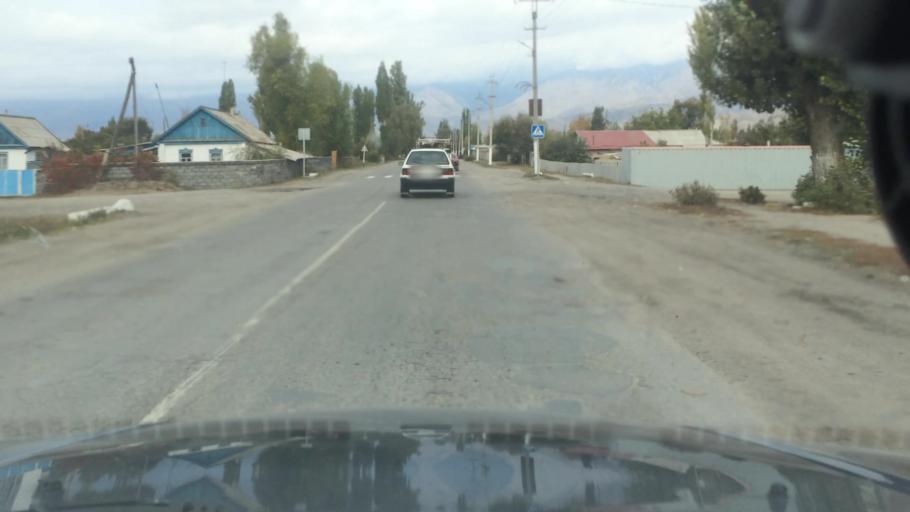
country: KG
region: Ysyk-Koel
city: Tyup
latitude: 42.7237
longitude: 78.3658
